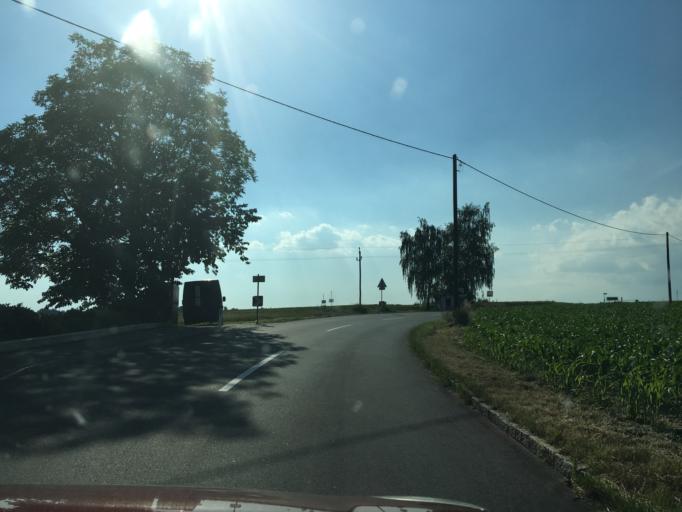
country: AT
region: Lower Austria
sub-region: Politischer Bezirk Amstetten
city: Ennsdorf
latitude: 48.2806
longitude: 14.5002
